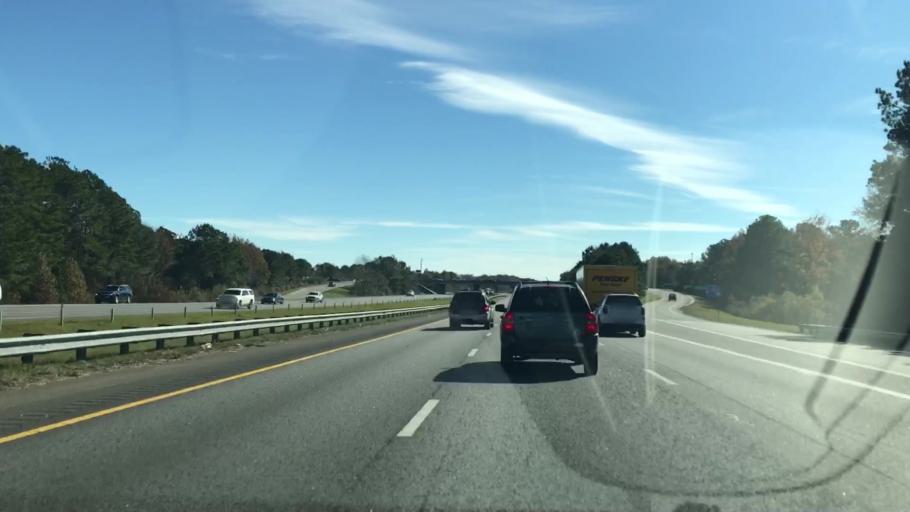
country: US
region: South Carolina
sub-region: Berkeley County
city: Ladson
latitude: 33.0012
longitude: -80.0971
